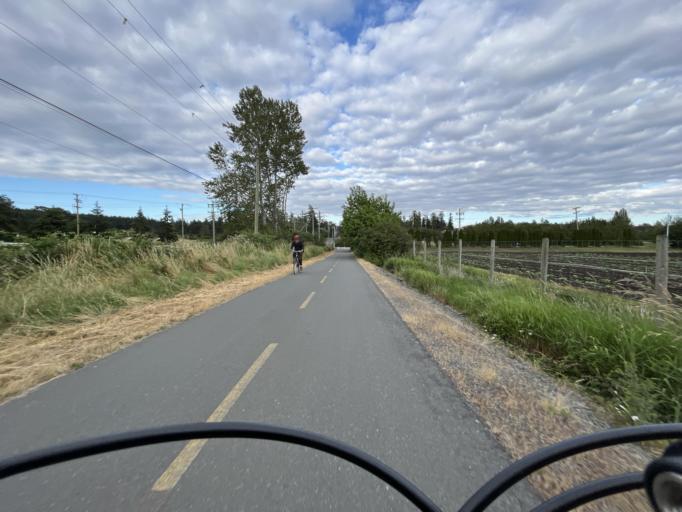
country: CA
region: British Columbia
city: Victoria
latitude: 48.4767
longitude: -123.3538
